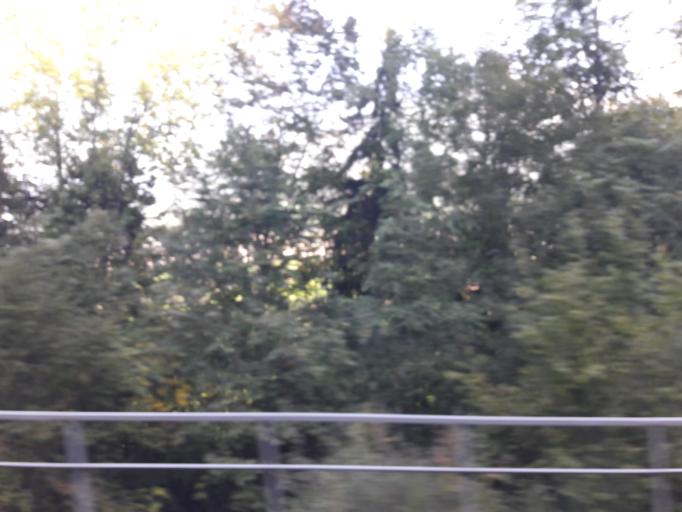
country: CH
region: Schwyz
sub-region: Bezirk Schwyz
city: Arth
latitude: 47.0534
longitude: 8.5195
